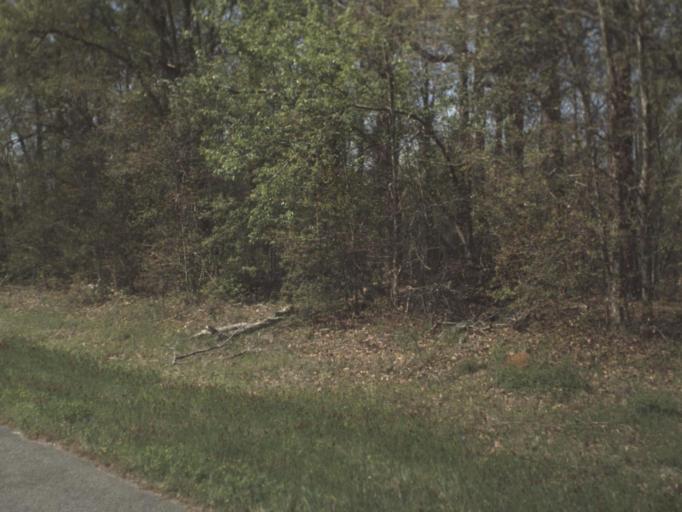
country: US
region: Florida
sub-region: Washington County
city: Chipley
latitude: 30.8345
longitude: -85.5029
